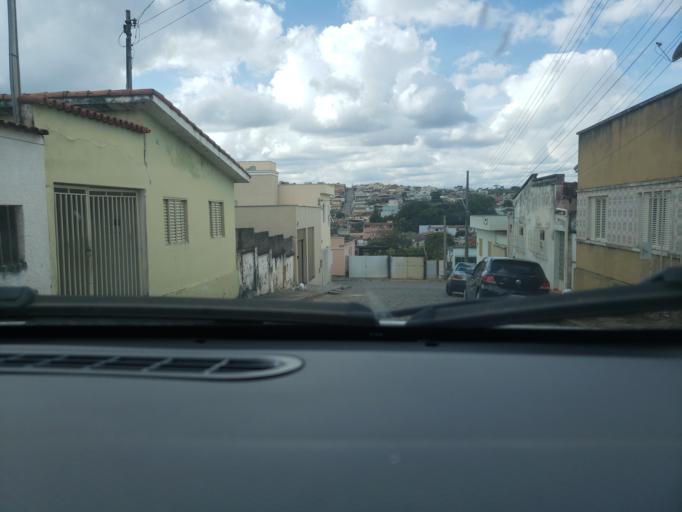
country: BR
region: Minas Gerais
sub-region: Campo Belo
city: Campo Belo
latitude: -20.8993
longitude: -45.2684
